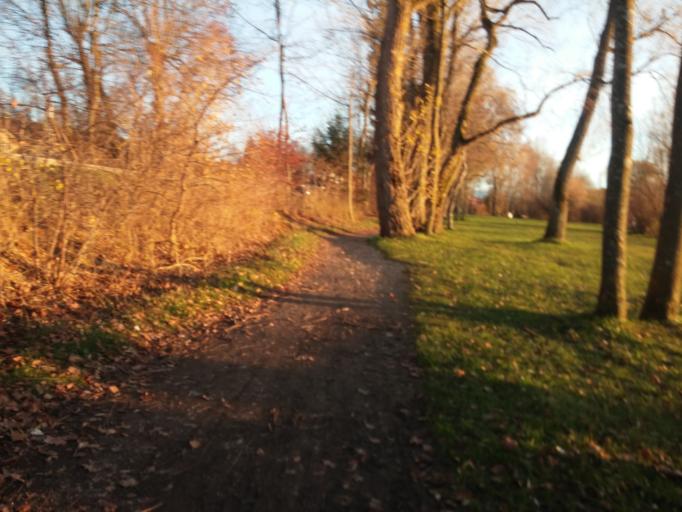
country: DE
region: Bavaria
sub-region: Upper Bavaria
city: Seeon-Seebruck
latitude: 47.9302
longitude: 12.4907
